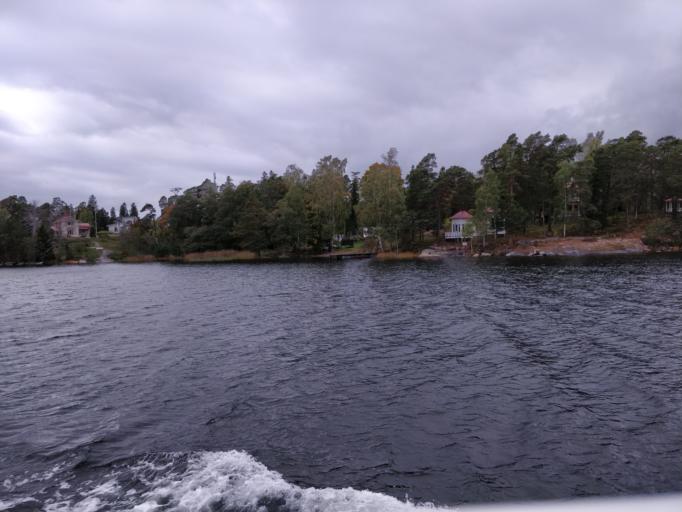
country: FI
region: Uusimaa
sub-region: Helsinki
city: Vantaa
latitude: 60.1609
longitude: 25.0993
